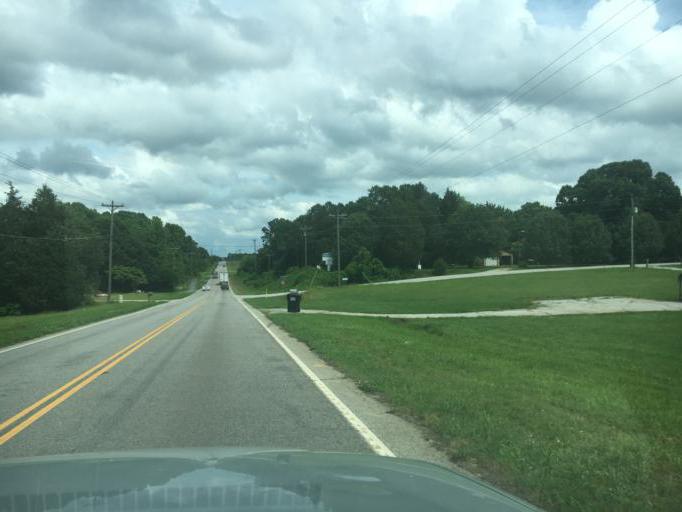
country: US
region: South Carolina
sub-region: Anderson County
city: Williamston
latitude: 34.6334
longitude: -82.4103
